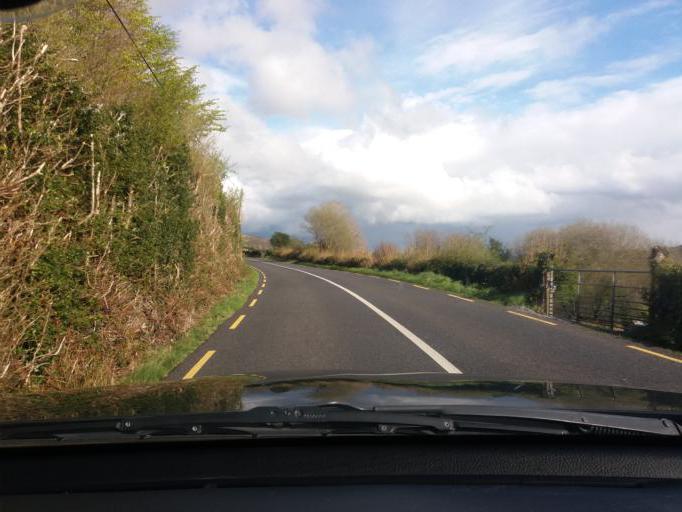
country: IE
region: Connaught
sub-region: County Leitrim
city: Kinlough
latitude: 54.3746
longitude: -8.2828
